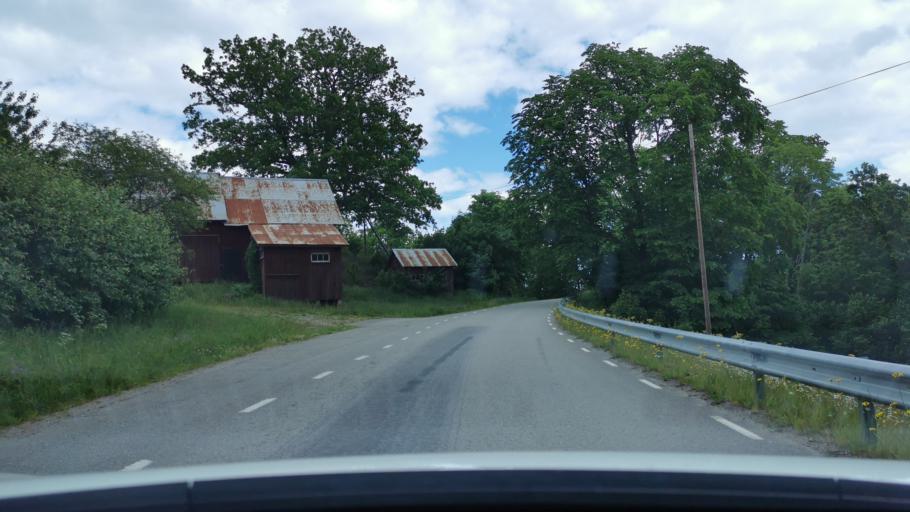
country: SE
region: Vaestra Goetaland
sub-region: Bengtsfors Kommun
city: Dals Langed
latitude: 58.8400
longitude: 12.3313
